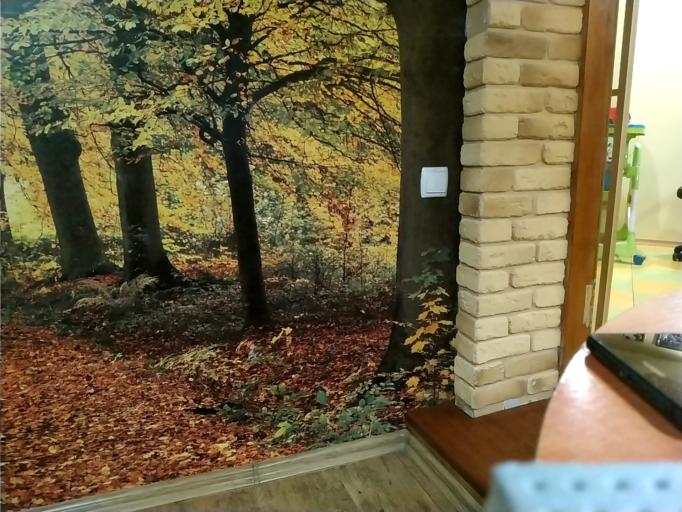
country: RU
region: Tverskaya
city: Zubtsov
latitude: 56.2517
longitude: 34.7003
